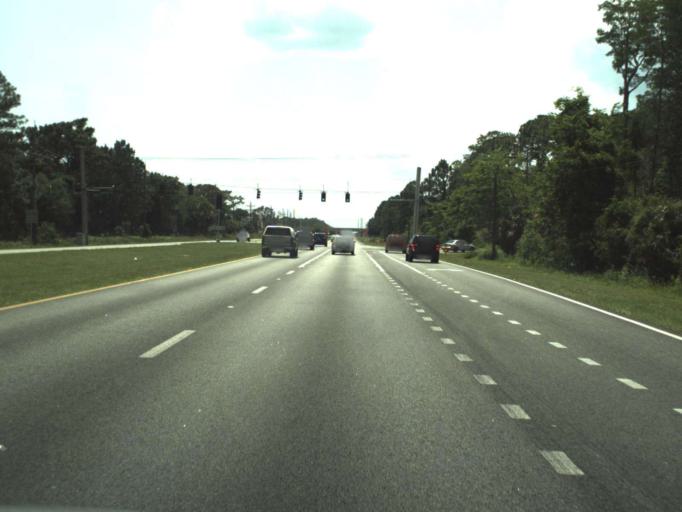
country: US
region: Florida
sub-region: Volusia County
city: Glencoe
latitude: 29.0131
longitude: -80.9783
